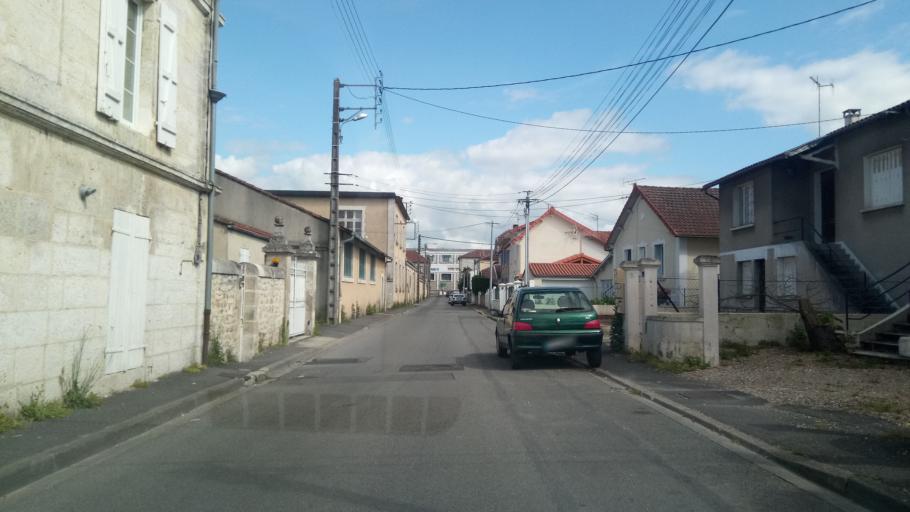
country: FR
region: Poitou-Charentes
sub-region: Departement de la Charente
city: Angouleme
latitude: 45.6479
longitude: 0.1419
